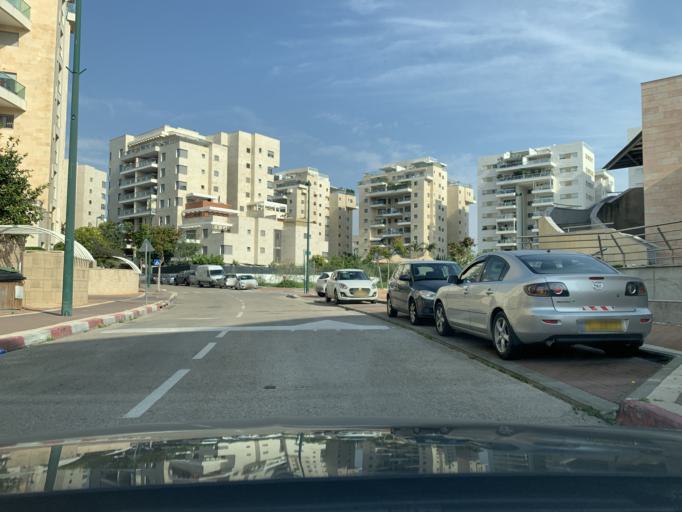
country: IL
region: Central District
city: Ganne Tiqwa
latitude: 32.0509
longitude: 34.8561
